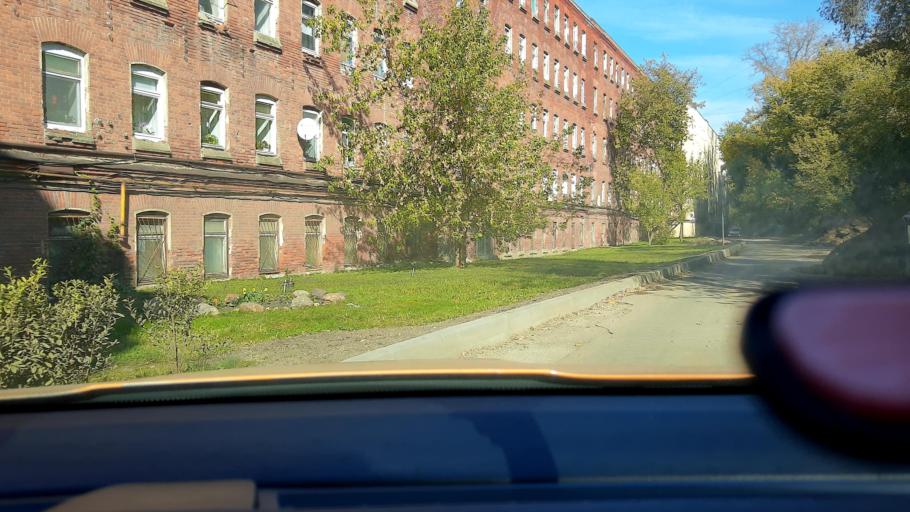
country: RU
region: Moscow
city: Strogino
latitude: 55.8391
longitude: 37.4125
